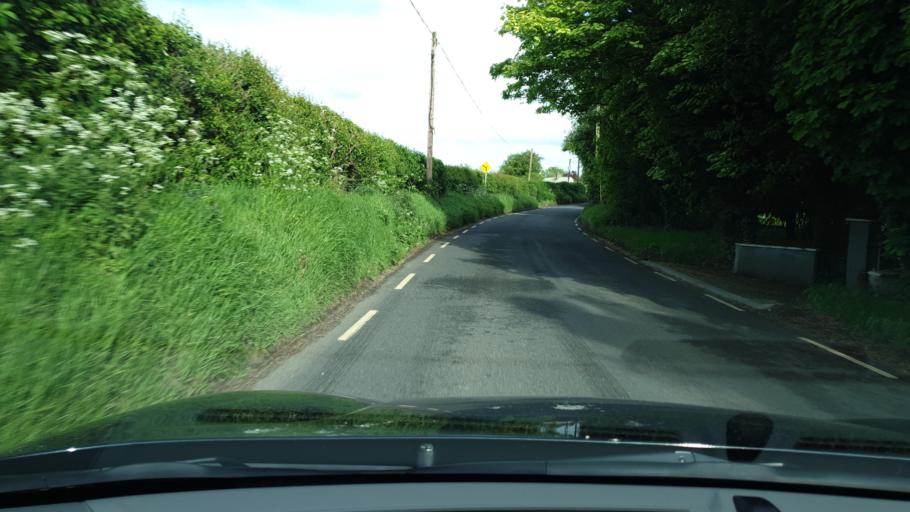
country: IE
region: Leinster
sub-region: An Mhi
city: Ashbourne
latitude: 53.5341
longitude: -6.3987
